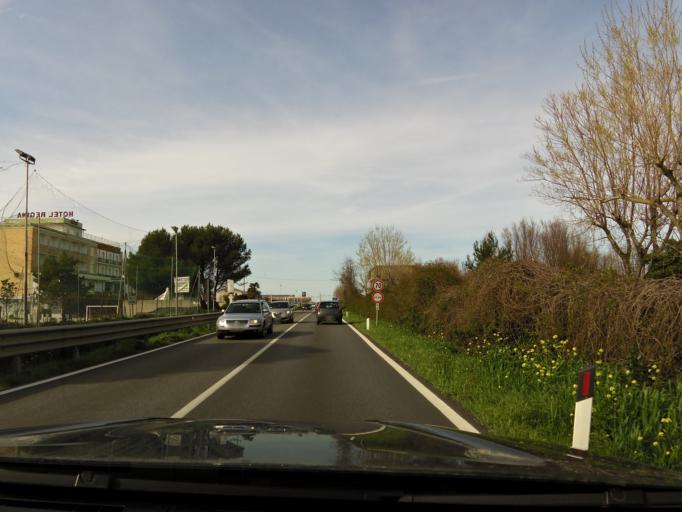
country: IT
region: The Marches
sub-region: Provincia di Macerata
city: Porto Recanati
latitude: 43.4052
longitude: 13.6775
